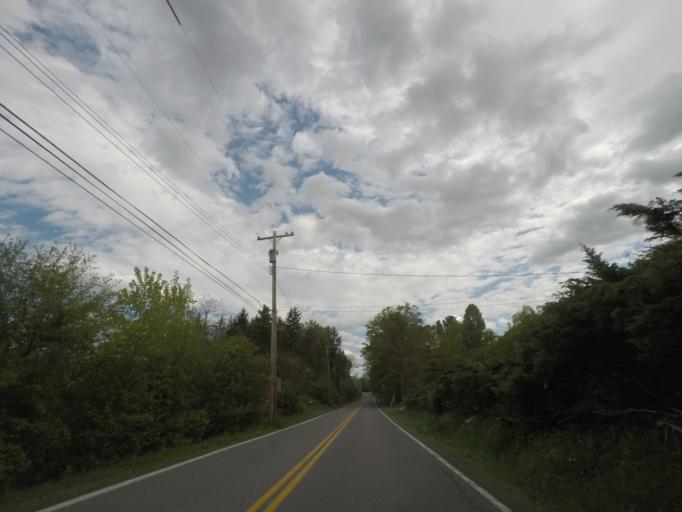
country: US
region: New York
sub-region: Albany County
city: Voorheesville
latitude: 42.6661
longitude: -73.9086
